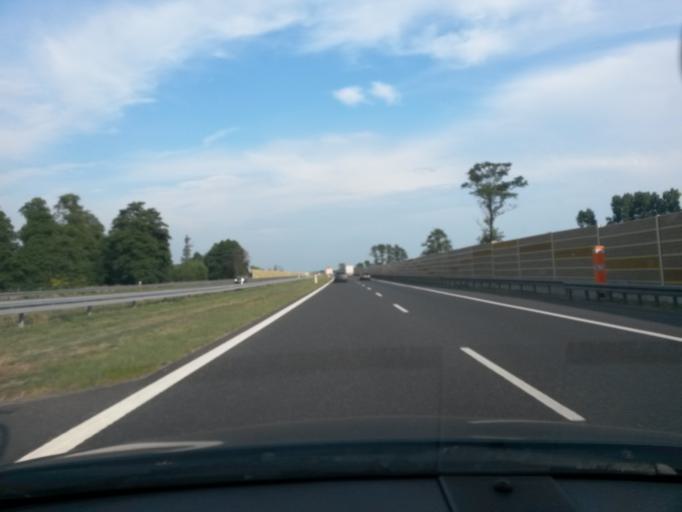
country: PL
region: Lodz Voivodeship
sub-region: Powiat poddebicki
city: Wartkowice
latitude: 51.9724
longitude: 19.0883
